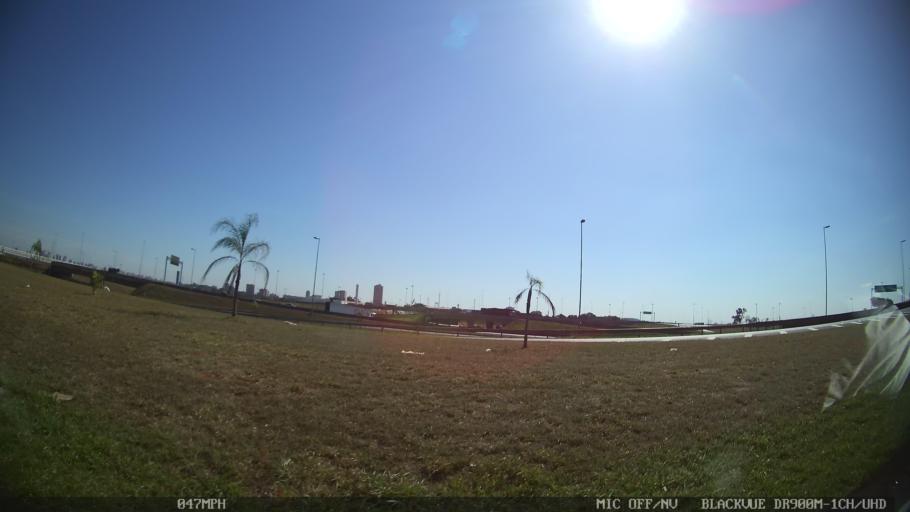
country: BR
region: Sao Paulo
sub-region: Ribeirao Preto
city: Ribeirao Preto
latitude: -21.2074
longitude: -47.7567
